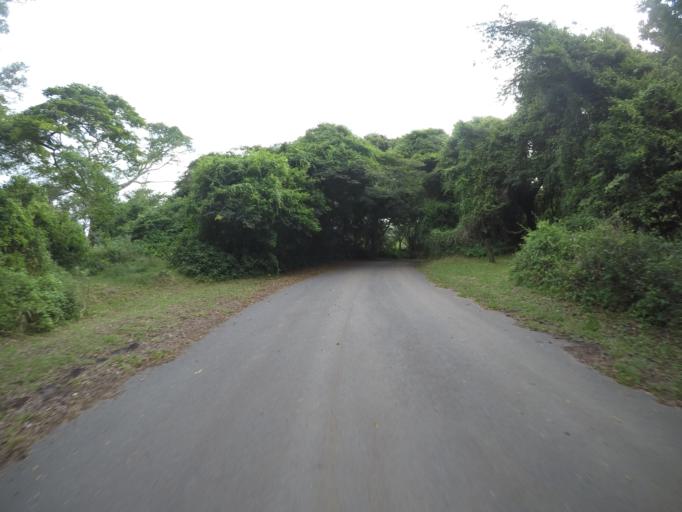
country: ZA
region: KwaZulu-Natal
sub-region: uMkhanyakude District Municipality
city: Mtubatuba
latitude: -28.3878
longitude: 32.4092
